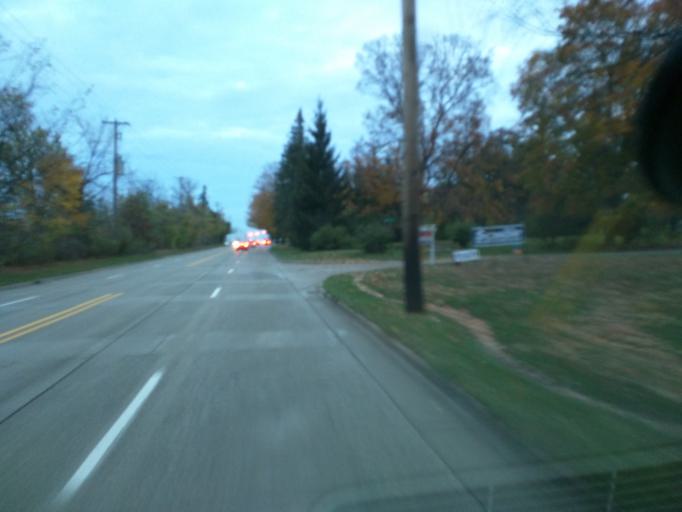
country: US
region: Michigan
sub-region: Eaton County
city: Waverly
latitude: 42.7114
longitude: -84.6030
